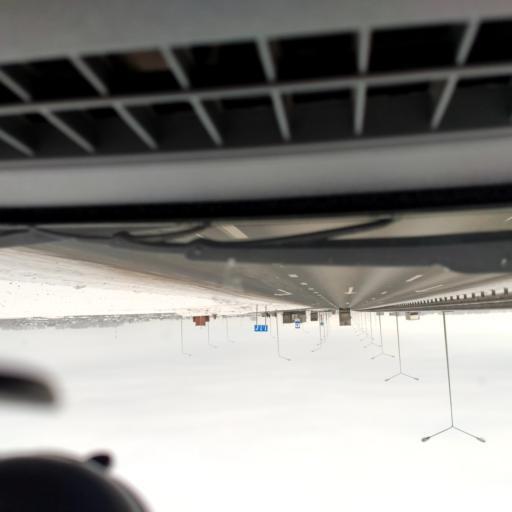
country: RU
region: Bashkortostan
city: Kushnarenkovo
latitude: 55.0722
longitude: 55.2895
